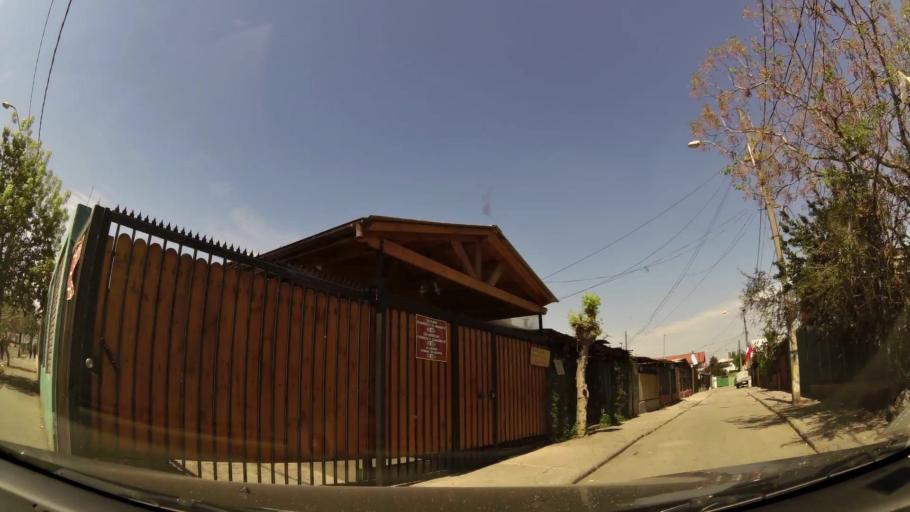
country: CL
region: Santiago Metropolitan
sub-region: Provincia de Santiago
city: La Pintana
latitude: -33.5916
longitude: -70.6266
